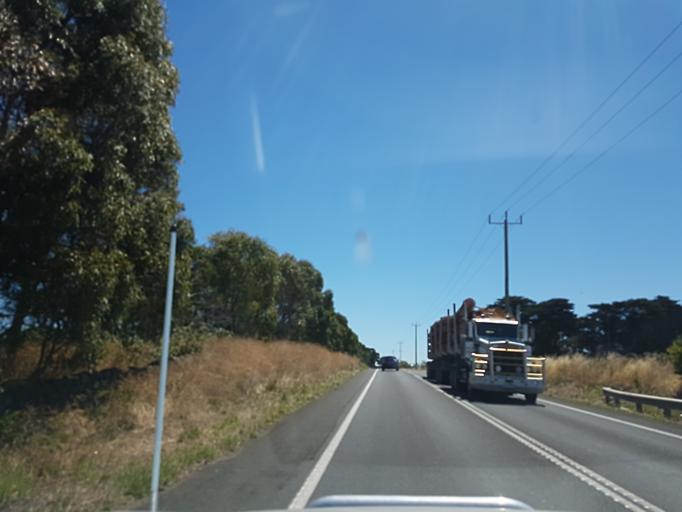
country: AU
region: Victoria
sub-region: Colac-Otway
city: Colac
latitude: -38.3411
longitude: 143.3732
